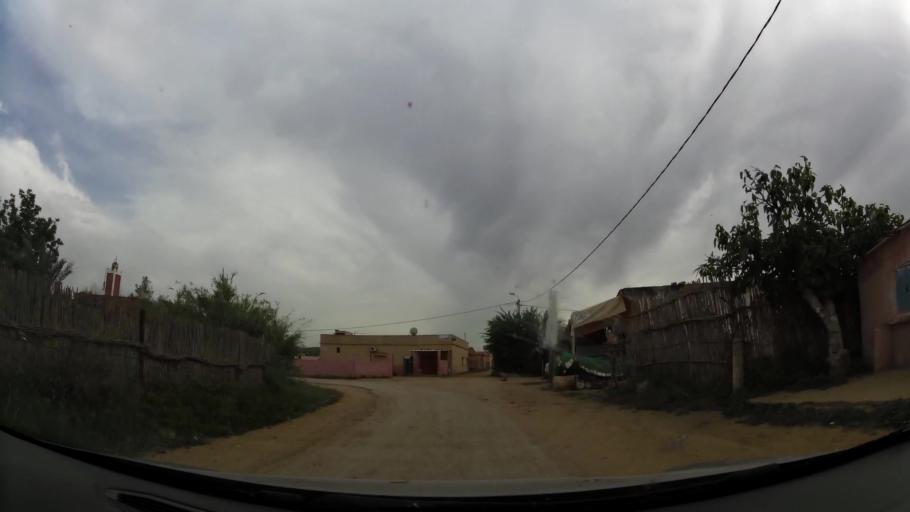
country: MA
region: Rabat-Sale-Zemmour-Zaer
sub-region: Khemisset
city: Khemisset
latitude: 33.7479
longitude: -6.2029
